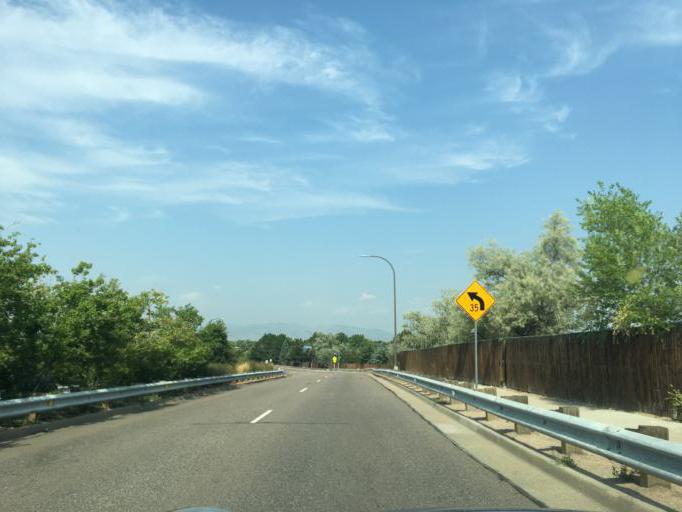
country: US
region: Colorado
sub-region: Adams County
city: Westminster
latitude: 39.8416
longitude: -105.0714
